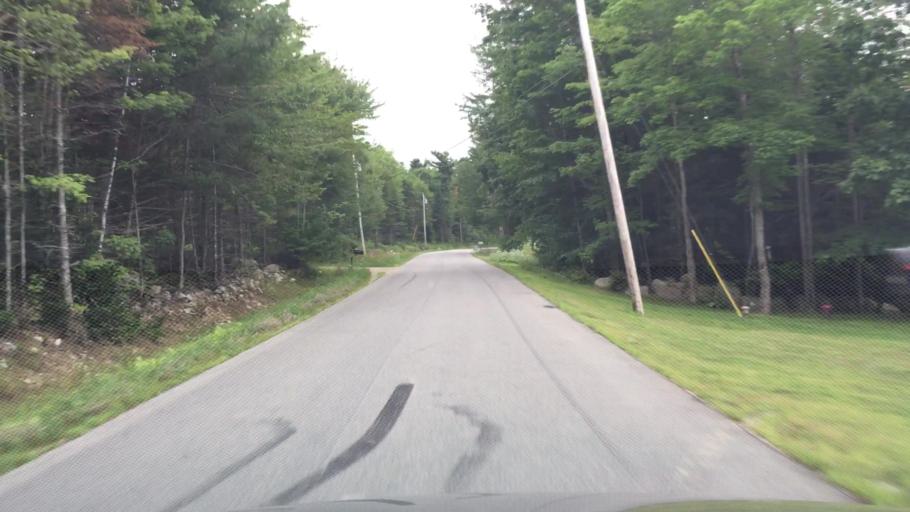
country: US
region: Maine
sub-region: Waldo County
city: Stockton Springs
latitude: 44.5159
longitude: -68.8758
